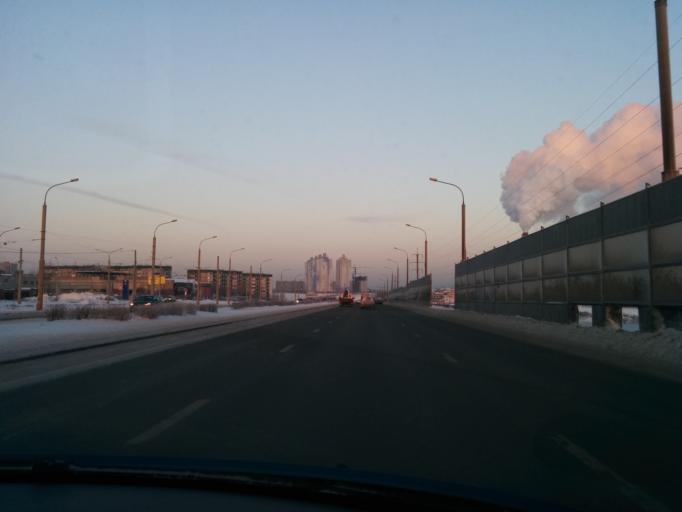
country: RU
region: Perm
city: Perm
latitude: 57.9957
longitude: 56.3068
